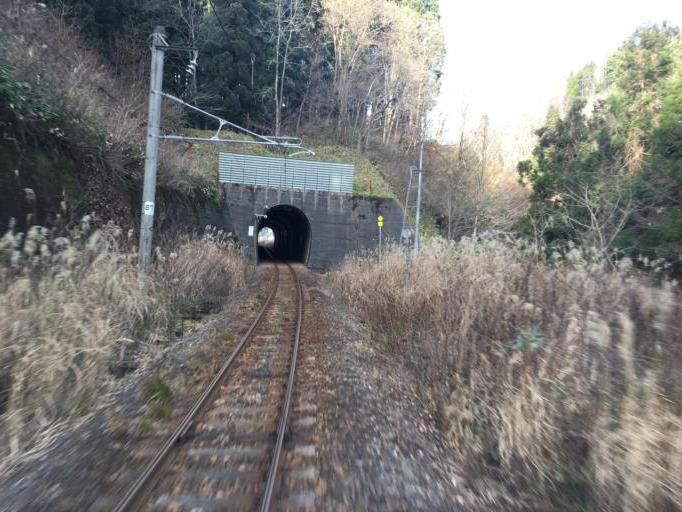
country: JP
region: Akita
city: Yuzawa
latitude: 38.9845
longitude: 140.3625
